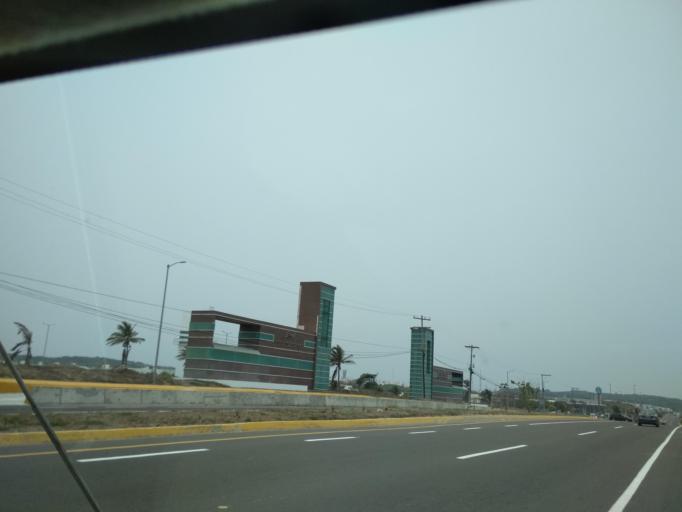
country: MX
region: Veracruz
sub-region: Alvarado
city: Playa de la Libertad
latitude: 19.0565
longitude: -96.0585
